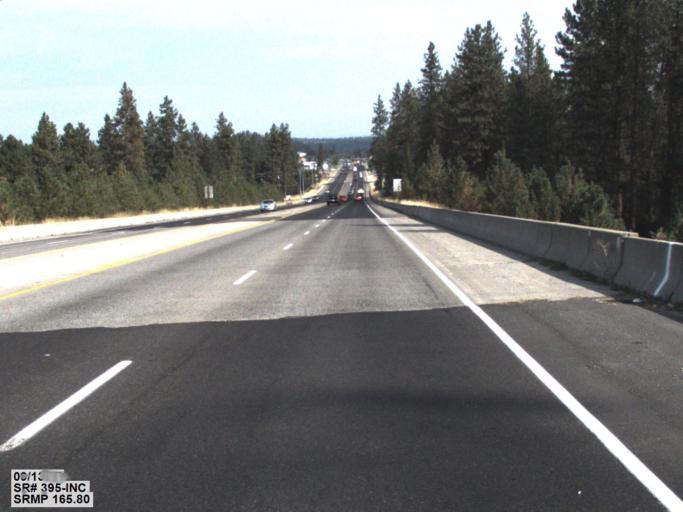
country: US
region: Washington
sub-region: Spokane County
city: Country Homes
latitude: 47.7579
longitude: -117.4085
